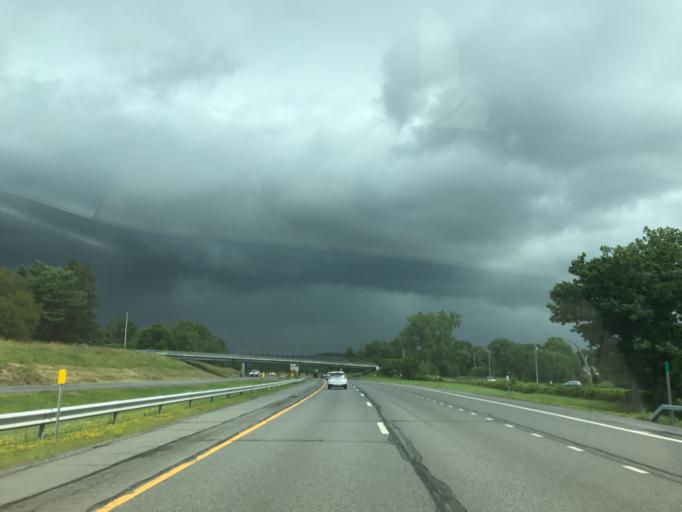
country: US
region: New York
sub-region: Albany County
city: Ravena
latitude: 42.4311
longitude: -73.8033
